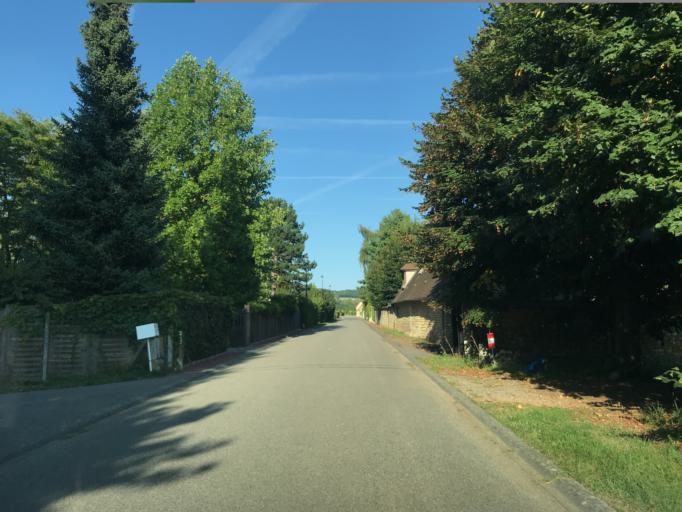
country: FR
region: Haute-Normandie
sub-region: Departement de l'Eure
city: Houlbec-Cocherel
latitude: 49.0536
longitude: 1.3068
